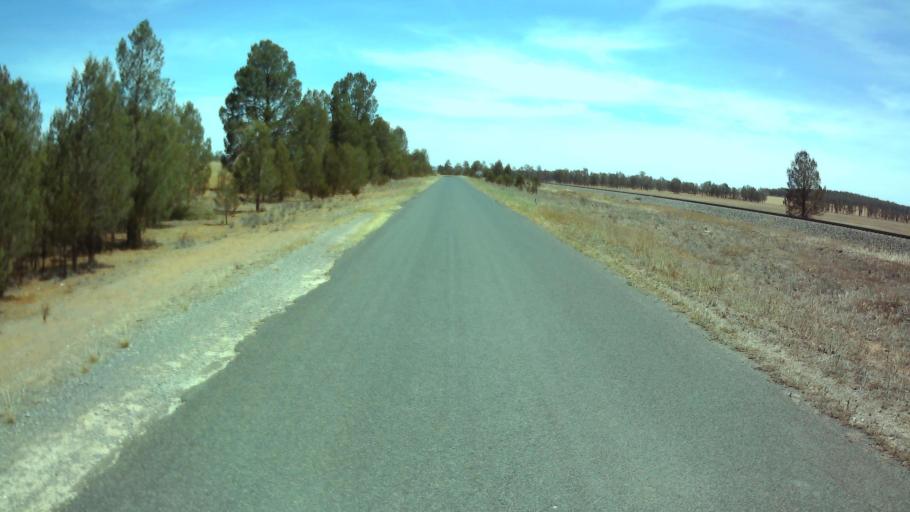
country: AU
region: New South Wales
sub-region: Weddin
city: Grenfell
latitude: -33.7744
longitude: 147.7555
